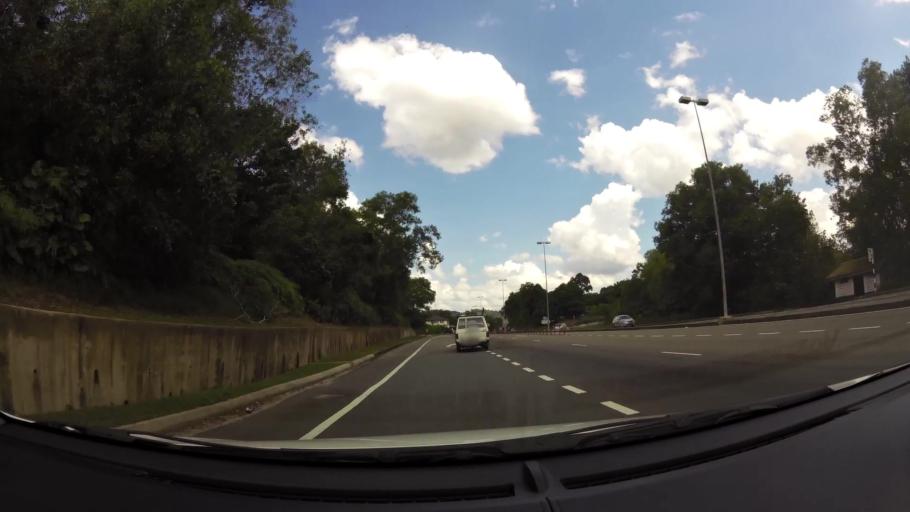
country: BN
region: Brunei and Muara
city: Bandar Seri Begawan
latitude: 4.9475
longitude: 114.9654
